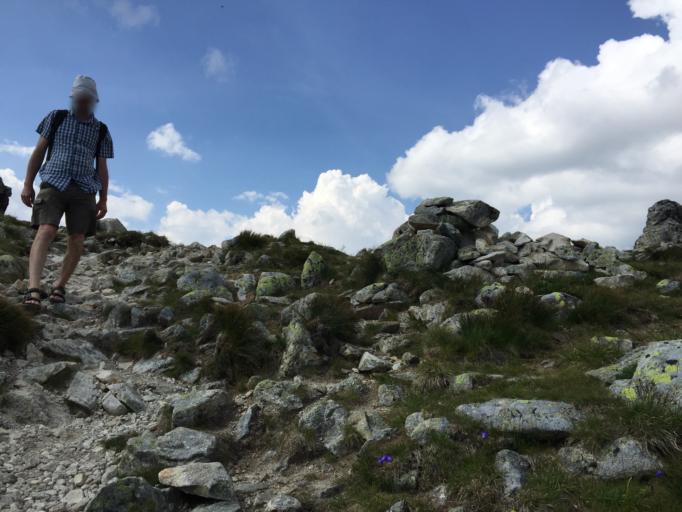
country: SK
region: Presovsky
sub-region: Okres Poprad
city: Vysoke Tatry
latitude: 49.1643
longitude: 20.2036
